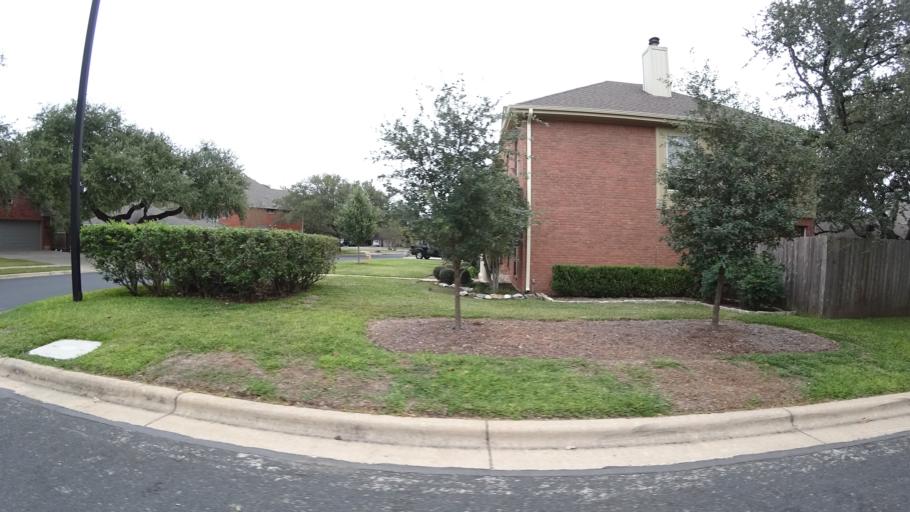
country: US
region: Texas
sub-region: Travis County
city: Shady Hollow
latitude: 30.1945
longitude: -97.8868
